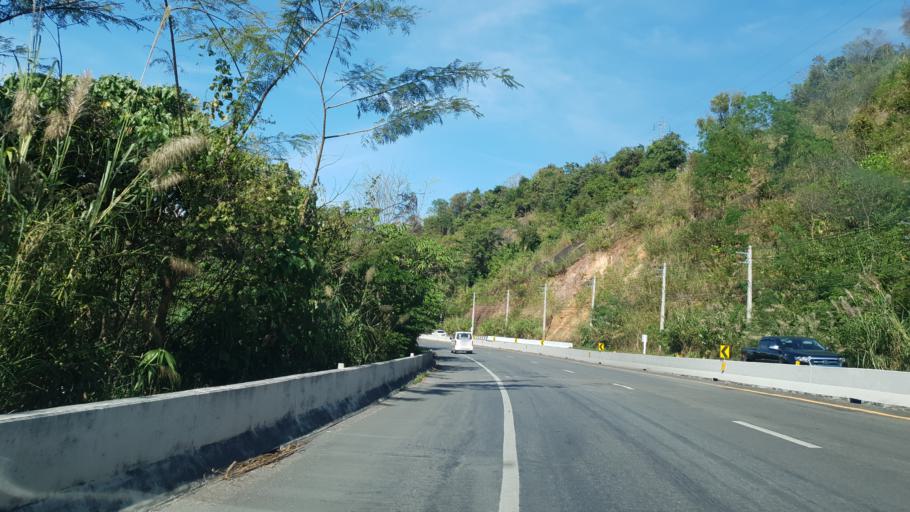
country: TH
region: Phrae
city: Den Chai
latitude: 17.8558
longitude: 100.0465
